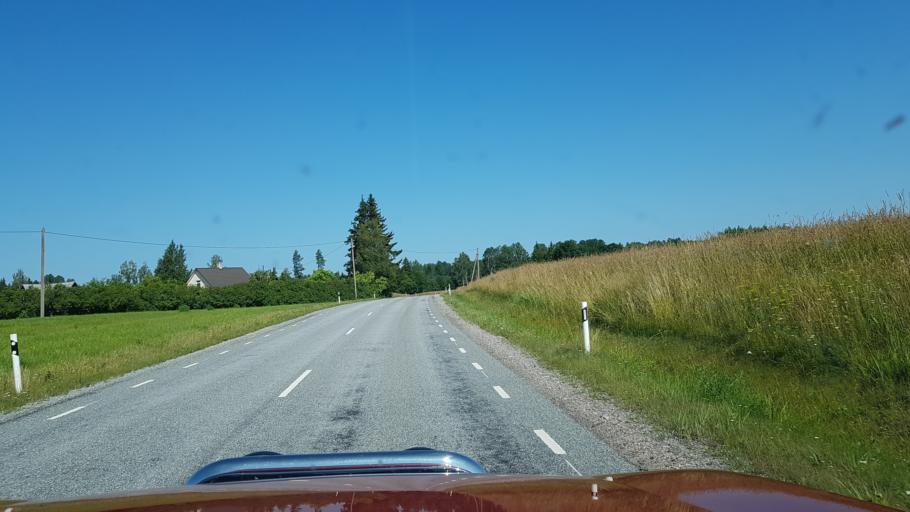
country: EE
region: Polvamaa
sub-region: Polva linn
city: Polva
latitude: 58.0827
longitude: 26.8343
